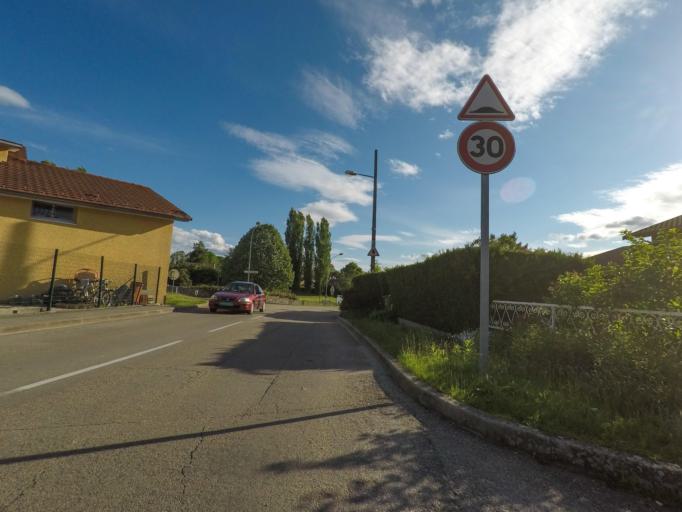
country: FR
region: Rhone-Alpes
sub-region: Departement de l'Ain
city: Saint-Genis-Pouilly
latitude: 46.2523
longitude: 6.0337
